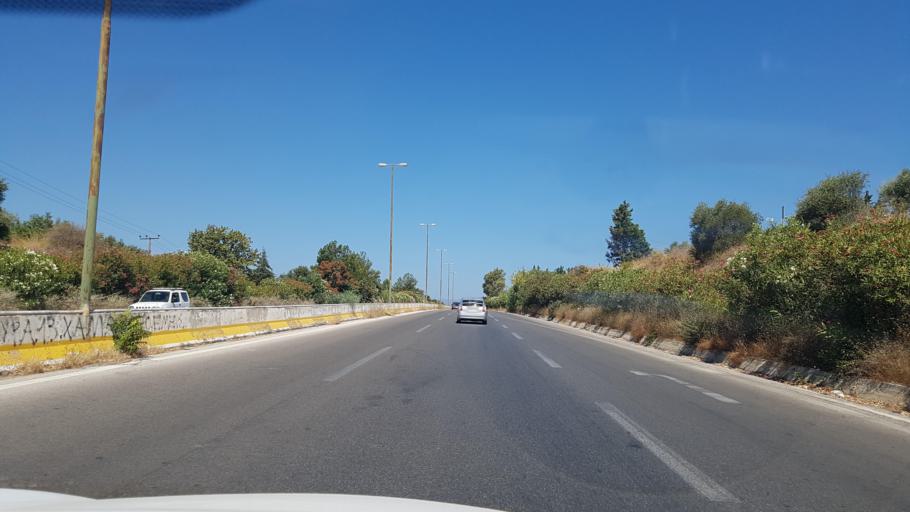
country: GR
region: Crete
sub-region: Nomos Chanias
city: Daratsos
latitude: 35.5000
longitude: 23.9893
